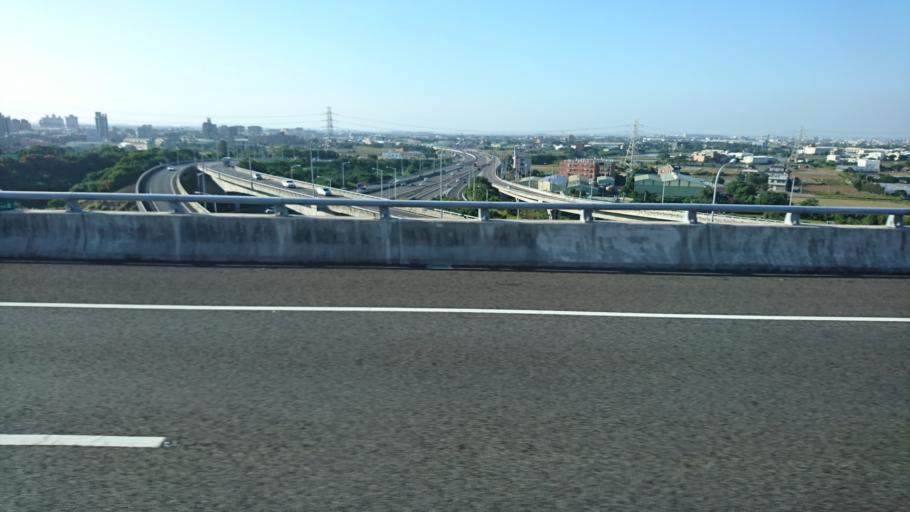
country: TW
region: Taiwan
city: Taoyuan City
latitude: 25.0197
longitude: 121.2738
